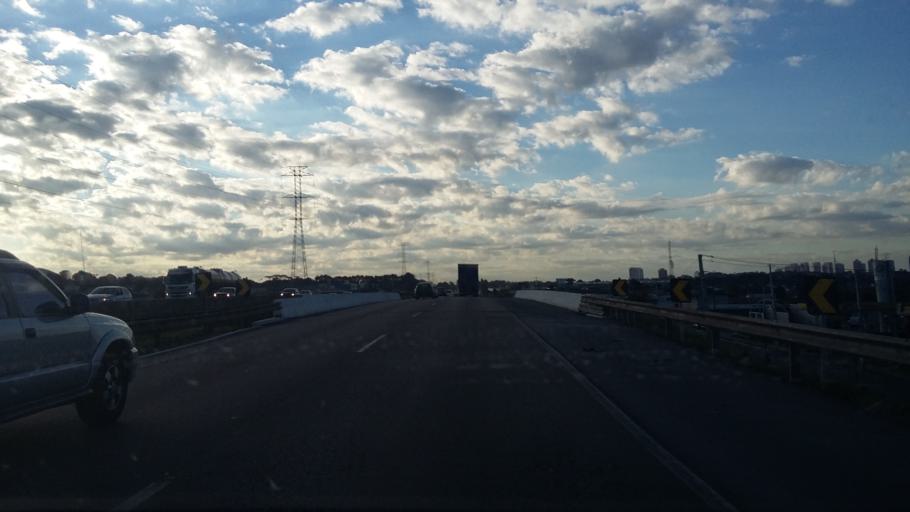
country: BR
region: Parana
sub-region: Curitiba
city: Curitiba
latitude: -25.4841
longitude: -49.3477
